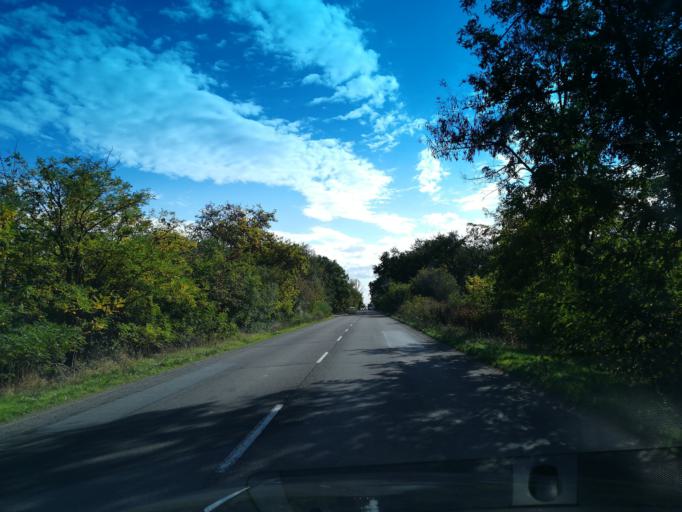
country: BG
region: Stara Zagora
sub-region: Obshtina Stara Zagora
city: Stara Zagora
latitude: 42.3541
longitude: 25.6577
